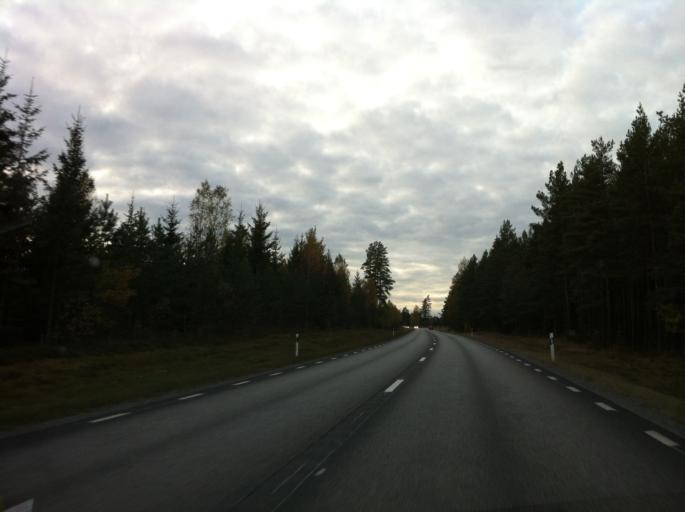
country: SE
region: OErebro
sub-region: Nora Kommun
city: Nora
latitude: 59.4608
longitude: 15.1306
